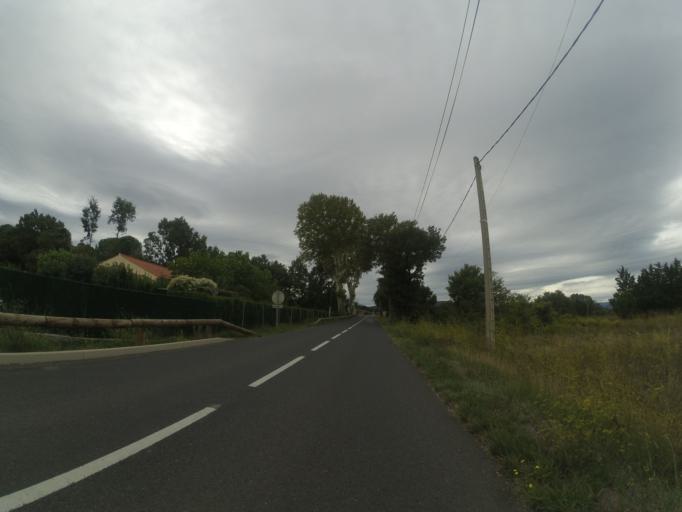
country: FR
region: Languedoc-Roussillon
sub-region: Departement des Pyrenees-Orientales
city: Estagel
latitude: 42.7684
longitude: 2.6934
